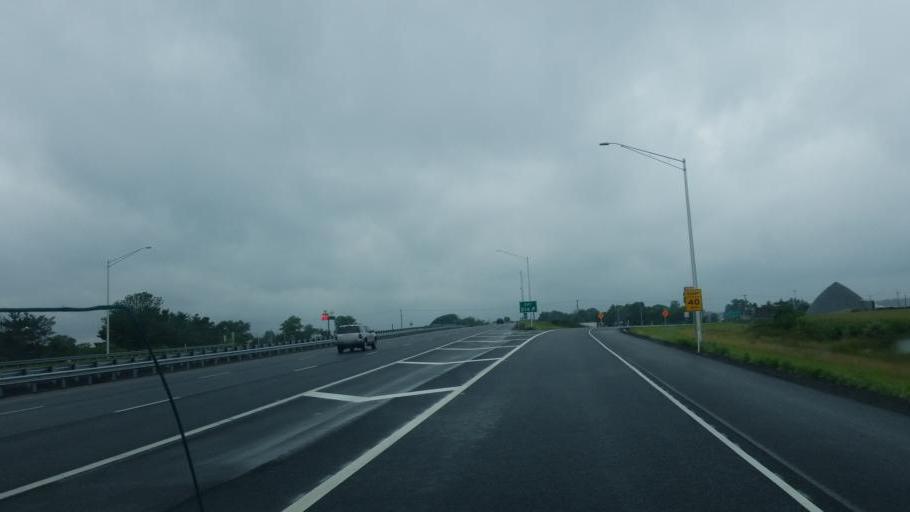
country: US
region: Indiana
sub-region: Madison County
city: Ingalls
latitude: 39.9934
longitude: -85.8388
